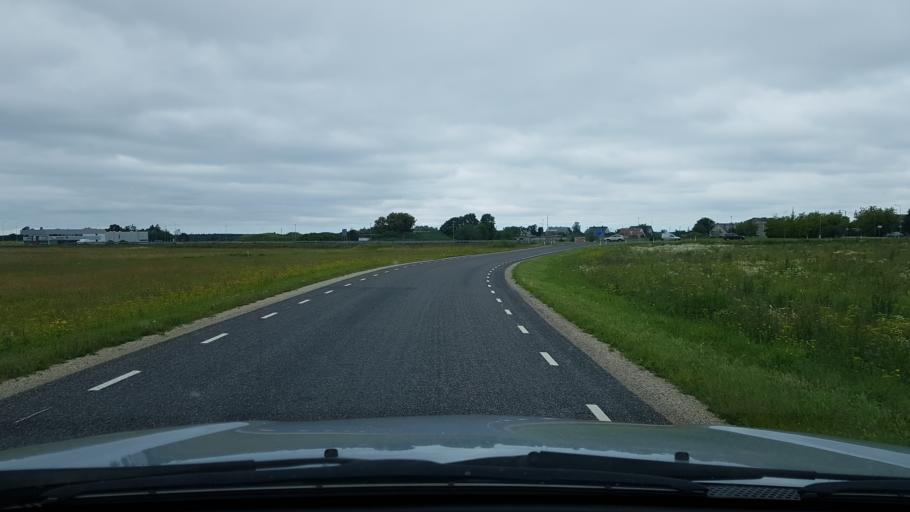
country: EE
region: Ida-Virumaa
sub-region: Narva linn
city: Narva
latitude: 59.3872
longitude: 28.1307
